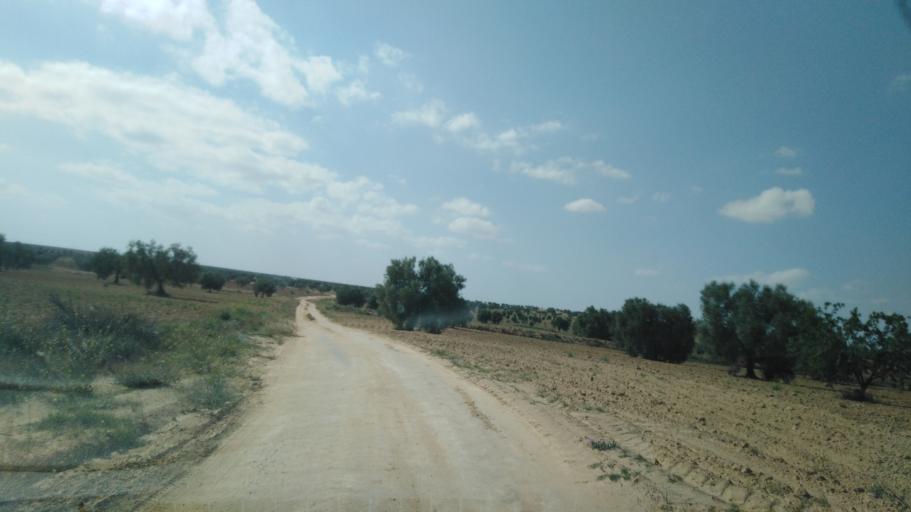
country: TN
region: Safaqis
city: Bi'r `Ali Bin Khalifah
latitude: 34.7975
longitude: 10.3890
